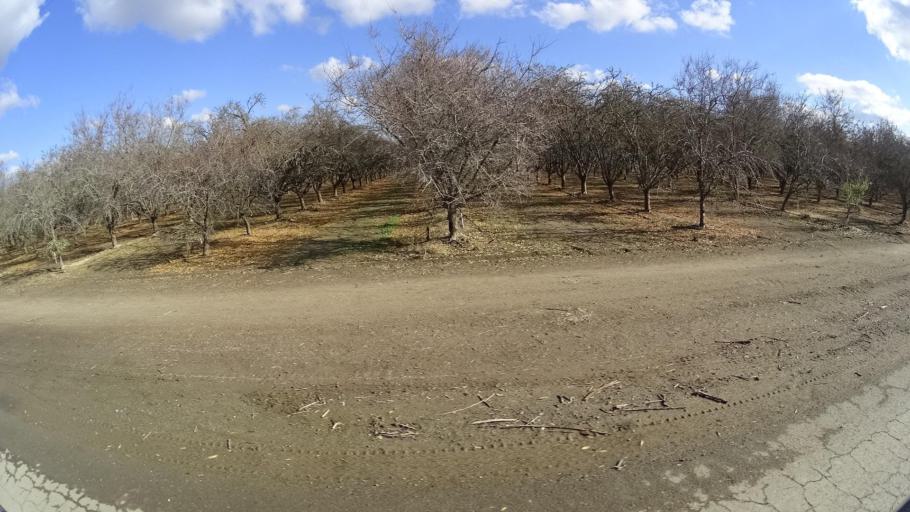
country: US
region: California
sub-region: Kern County
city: Delano
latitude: 35.7336
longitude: -119.3658
